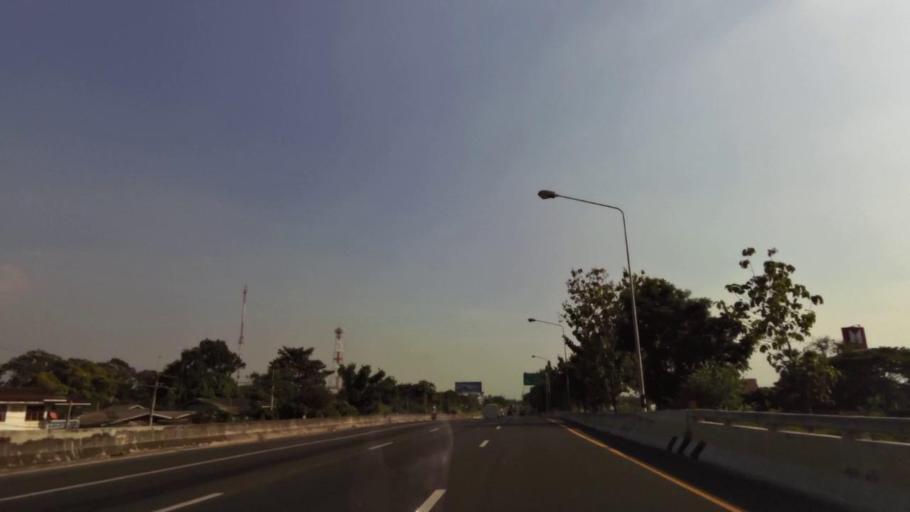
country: TH
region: Ang Thong
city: Ang Thong
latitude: 14.5972
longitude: 100.4735
